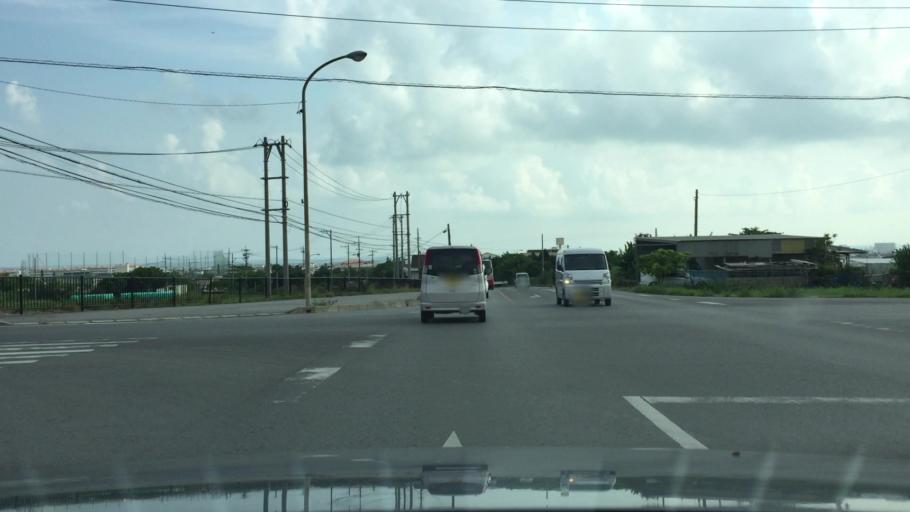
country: JP
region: Okinawa
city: Ishigaki
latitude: 24.3525
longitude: 124.1736
